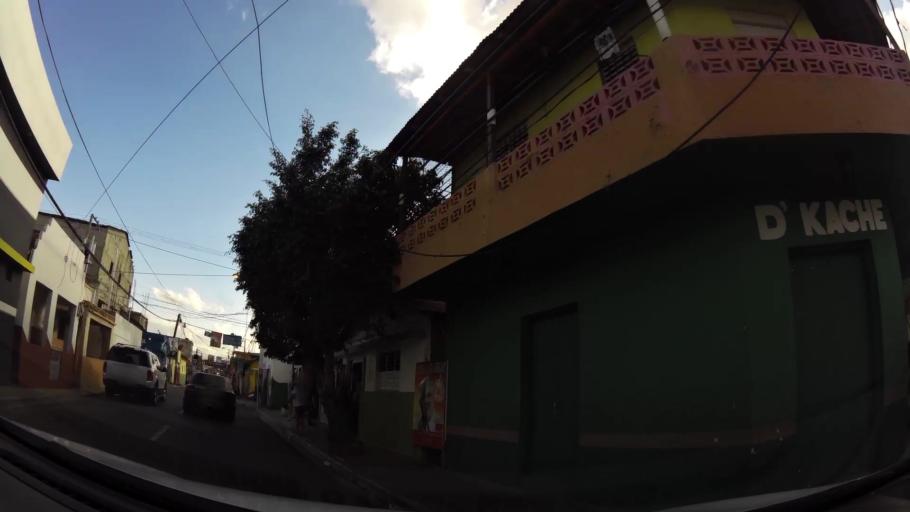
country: DO
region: Santiago
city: Santiago de los Caballeros
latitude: 19.4618
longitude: -70.7067
